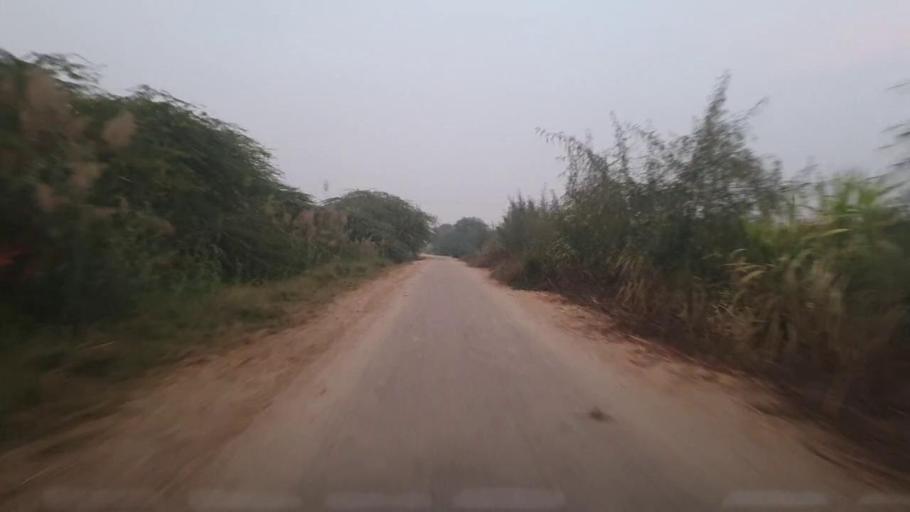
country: PK
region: Sindh
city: Gambat
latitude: 27.3432
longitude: 68.6105
